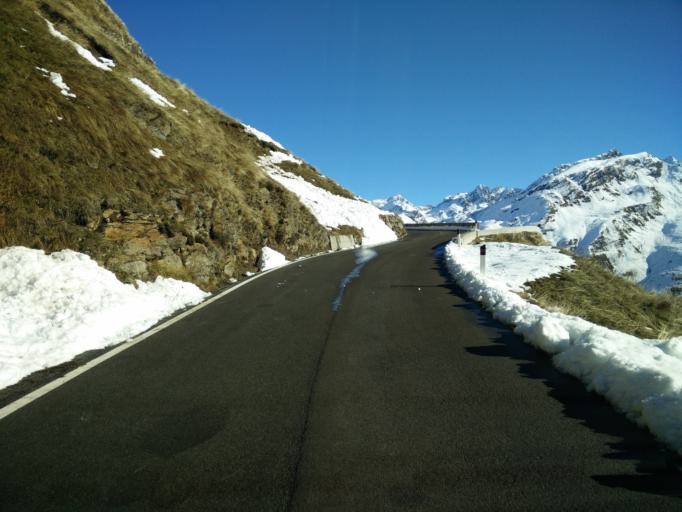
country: IT
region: Trentino-Alto Adige
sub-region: Bolzano
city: Moso in Passiria
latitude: 46.8889
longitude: 11.1194
